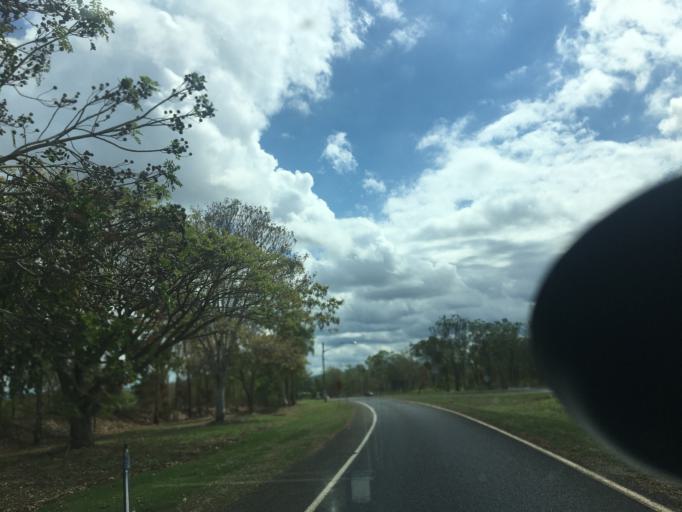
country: AU
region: Queensland
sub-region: Tablelands
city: Mareeba
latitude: -17.0108
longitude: 145.4307
